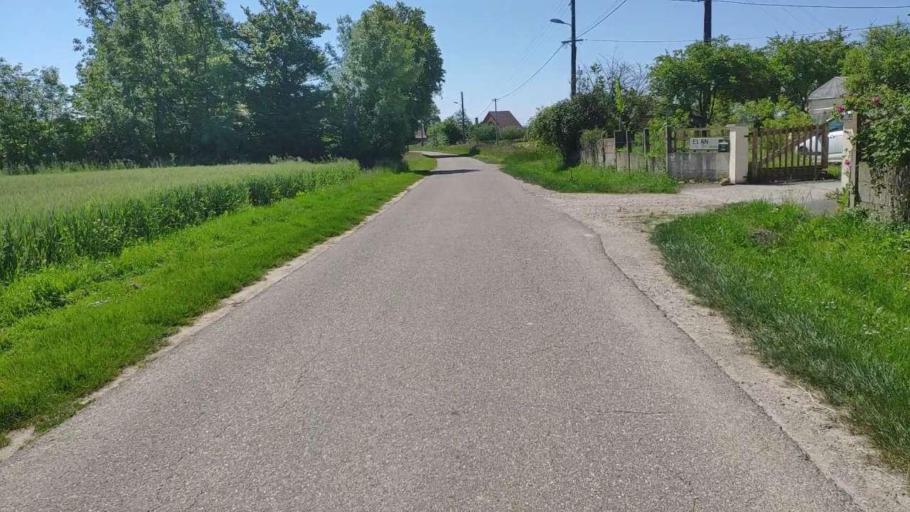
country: FR
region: Franche-Comte
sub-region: Departement du Jura
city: Bletterans
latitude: 46.7677
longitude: 5.4088
